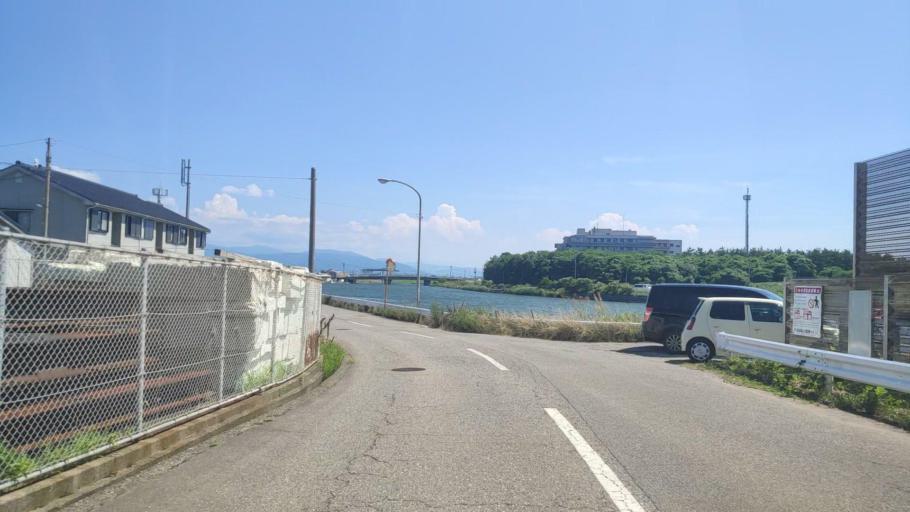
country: JP
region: Ishikawa
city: Kanazawa-shi
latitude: 36.6015
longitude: 136.5881
